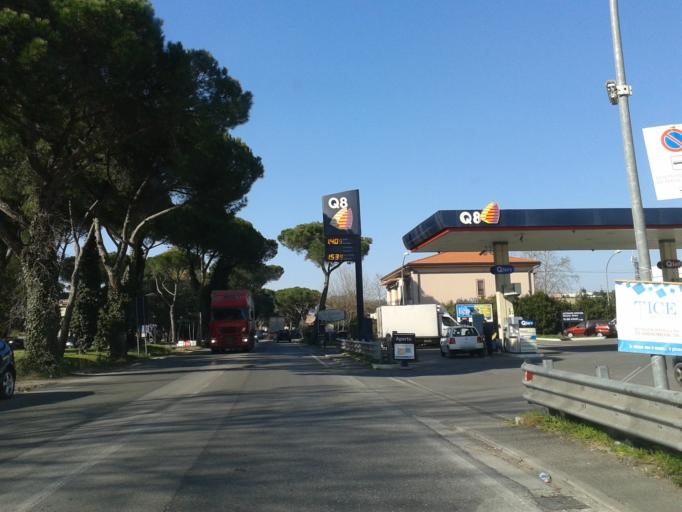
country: IT
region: Tuscany
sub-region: Province of Pisa
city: Pisa
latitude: 43.7176
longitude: 10.3819
